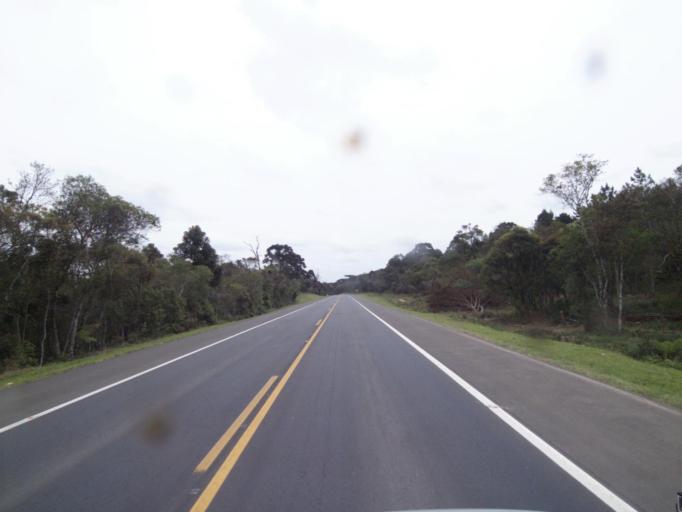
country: BR
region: Parana
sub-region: Irati
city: Irati
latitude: -25.4675
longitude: -50.5094
